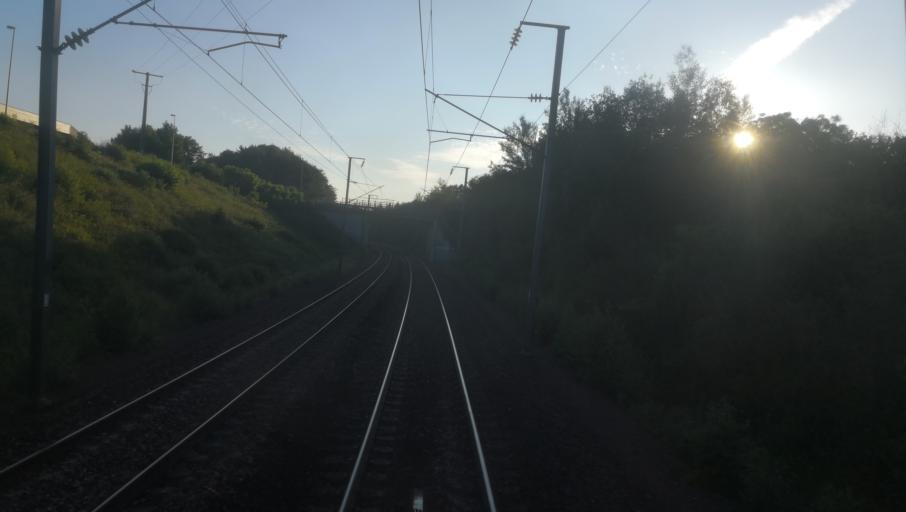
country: FR
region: Lower Normandy
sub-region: Departement du Calvados
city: Beuvillers
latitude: 49.1264
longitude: 0.2851
